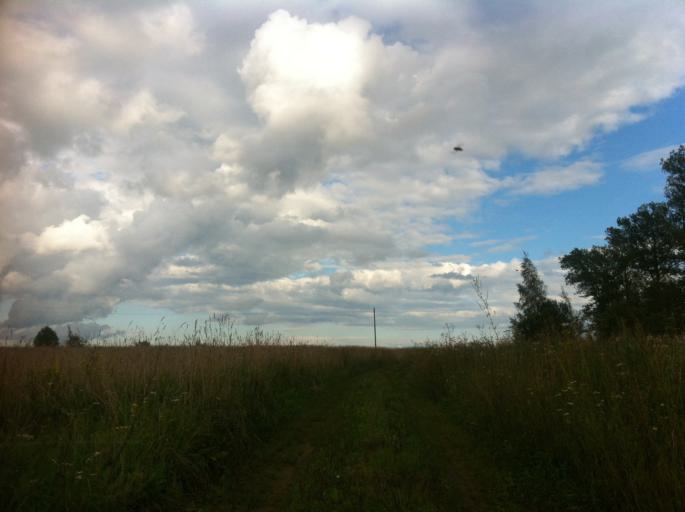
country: RU
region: Pskov
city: Izborsk
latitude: 57.8183
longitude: 27.9755
